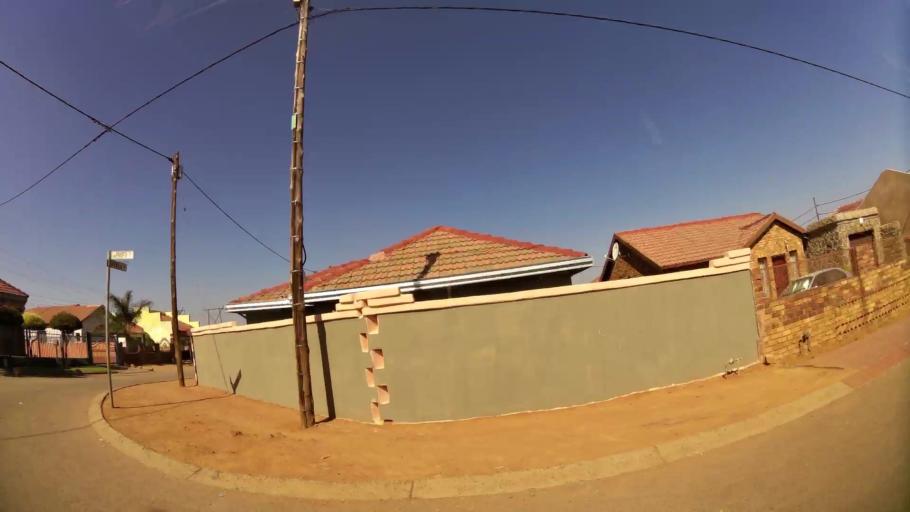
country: ZA
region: Gauteng
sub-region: City of Tshwane Metropolitan Municipality
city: Mabopane
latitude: -25.5584
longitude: 28.0817
